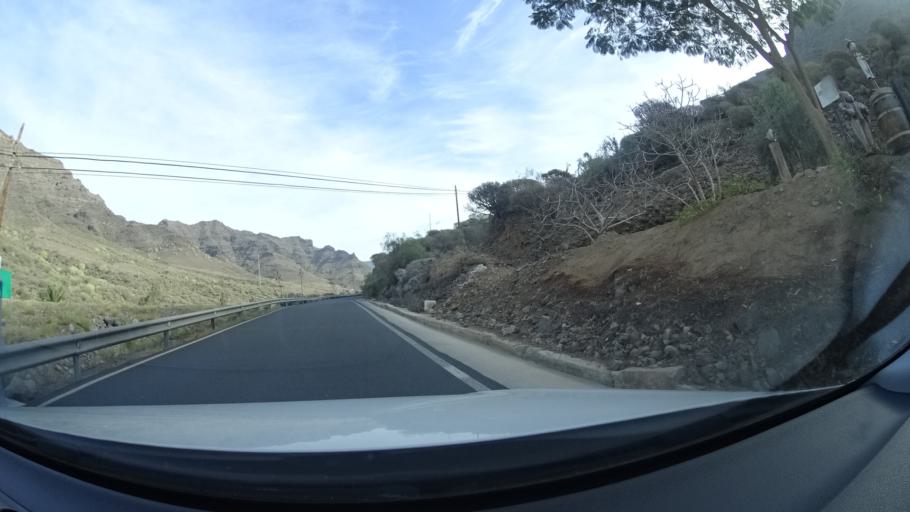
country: ES
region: Canary Islands
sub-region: Provincia de Las Palmas
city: Mogan
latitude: 27.8660
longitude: -15.7404
